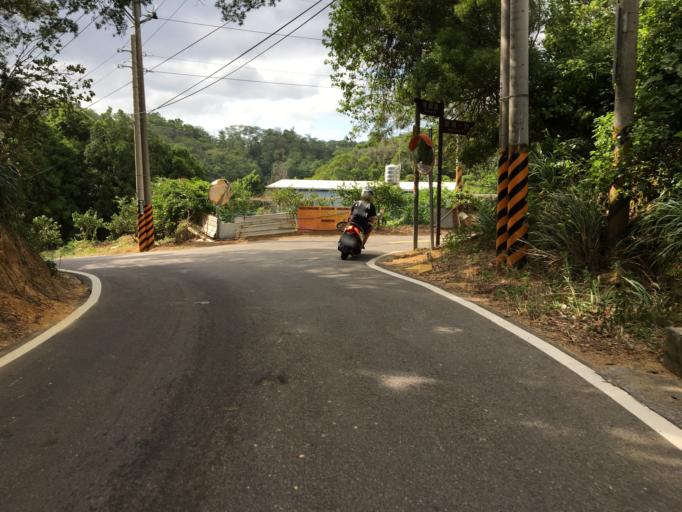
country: TW
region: Taiwan
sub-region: Hsinchu
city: Hsinchu
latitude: 24.7045
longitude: 120.9530
